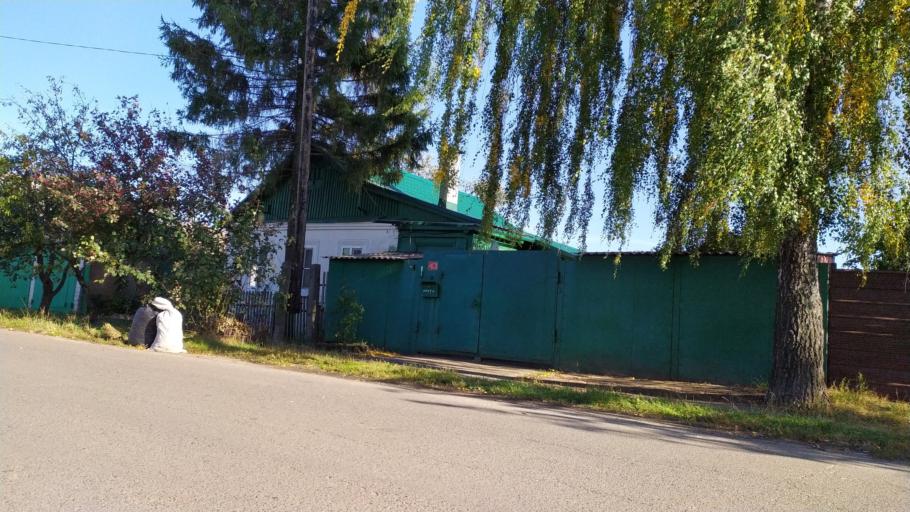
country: RU
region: Kursk
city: Kursk
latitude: 51.6447
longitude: 36.1454
